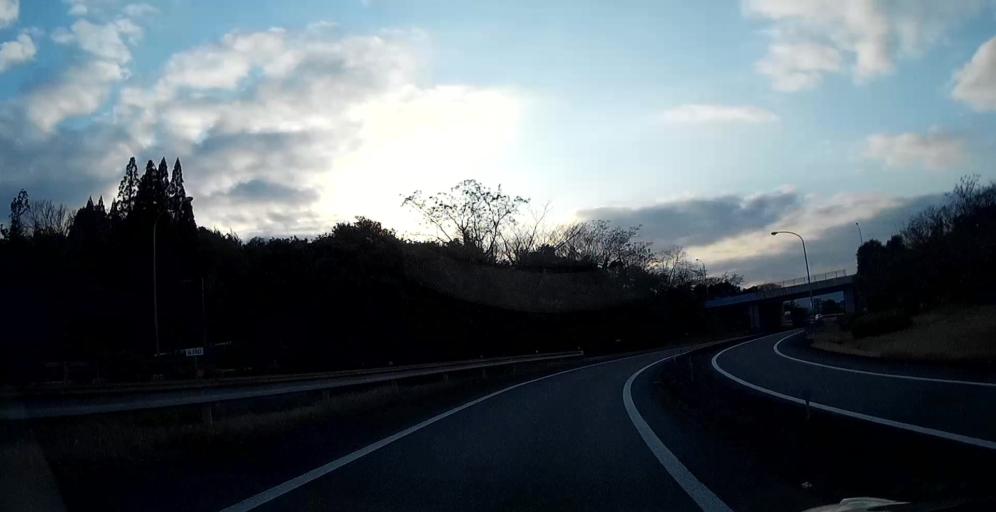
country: JP
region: Kumamoto
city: Matsubase
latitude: 32.6480
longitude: 130.7093
